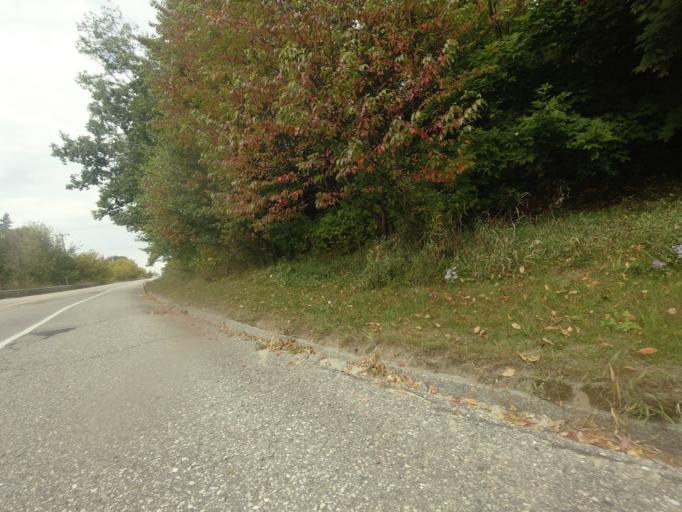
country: CA
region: Quebec
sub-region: Outaouais
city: Wakefield
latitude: 45.9479
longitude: -75.9485
